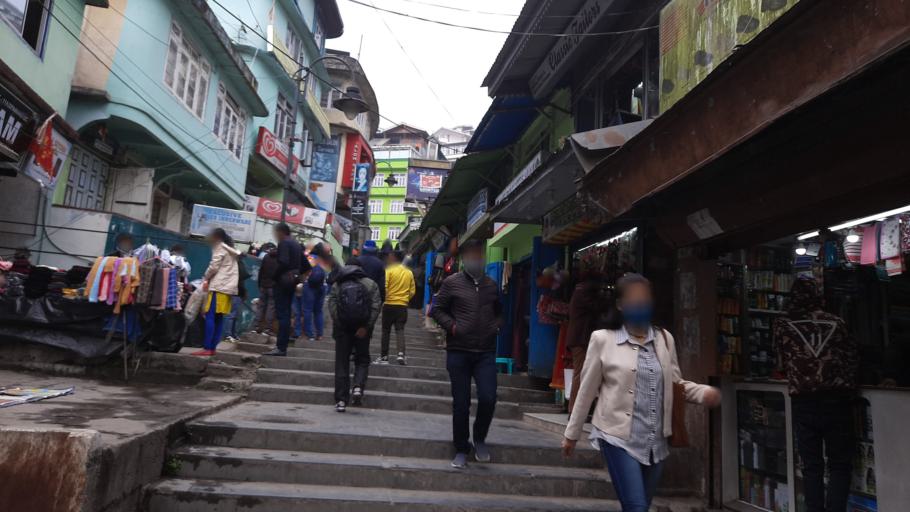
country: IN
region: Sikkim
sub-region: East District
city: Gangtok
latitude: 27.3272
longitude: 88.6123
